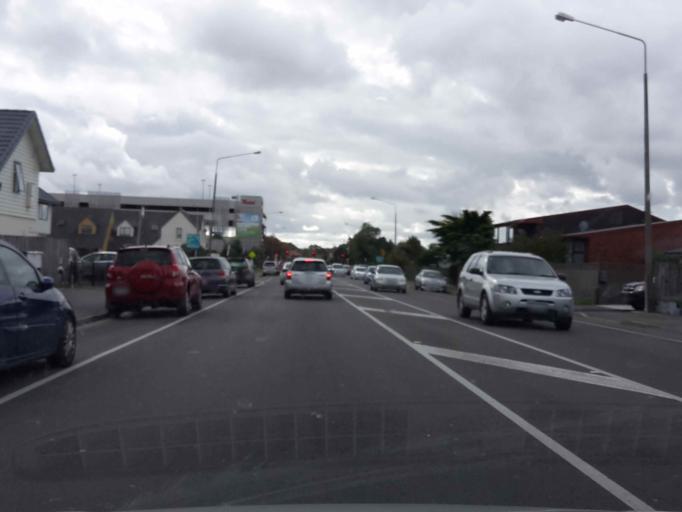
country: NZ
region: Canterbury
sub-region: Christchurch City
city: Christchurch
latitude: -43.5336
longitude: 172.6024
